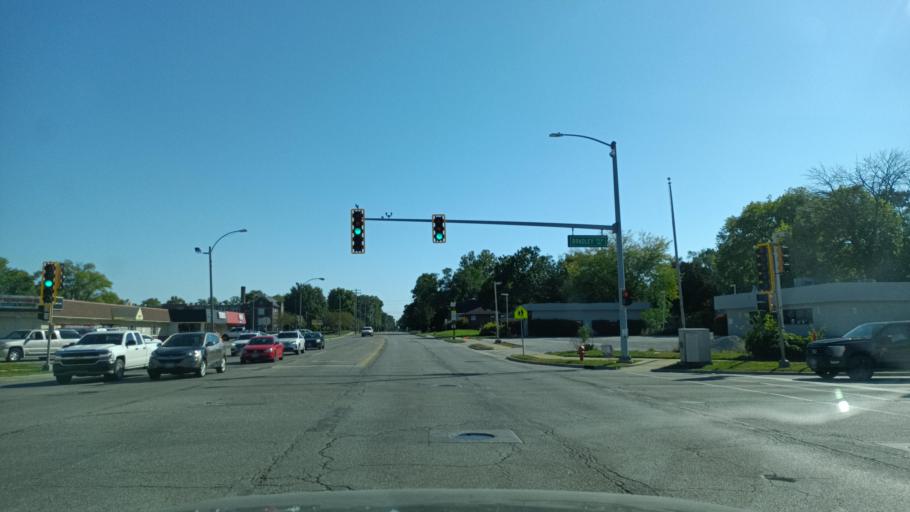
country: US
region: Illinois
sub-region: Champaign County
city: Champaign
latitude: 40.1274
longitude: -88.2580
